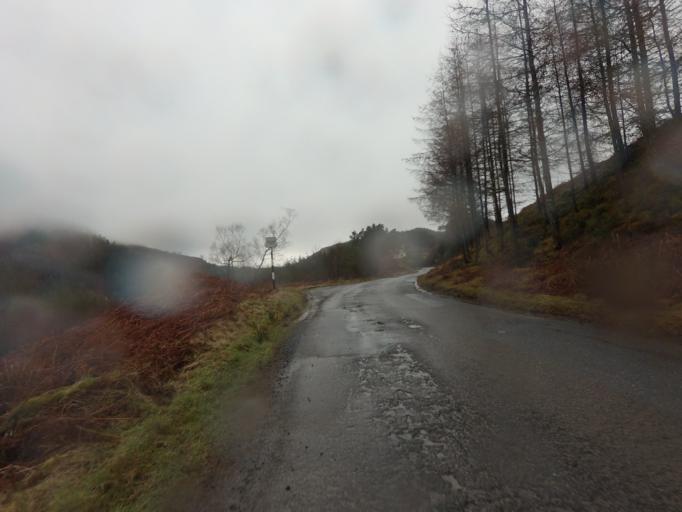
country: GB
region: Scotland
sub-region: West Dunbartonshire
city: Balloch
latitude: 56.2346
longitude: -4.5610
